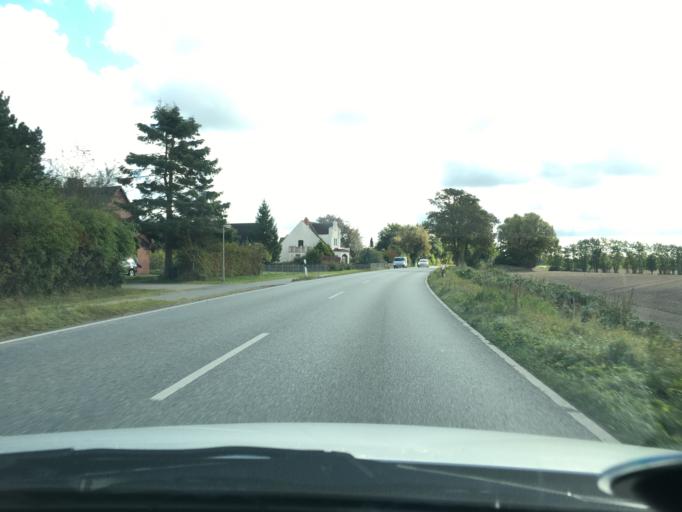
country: DE
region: Schleswig-Holstein
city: Krokau
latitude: 54.4075
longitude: 10.3471
